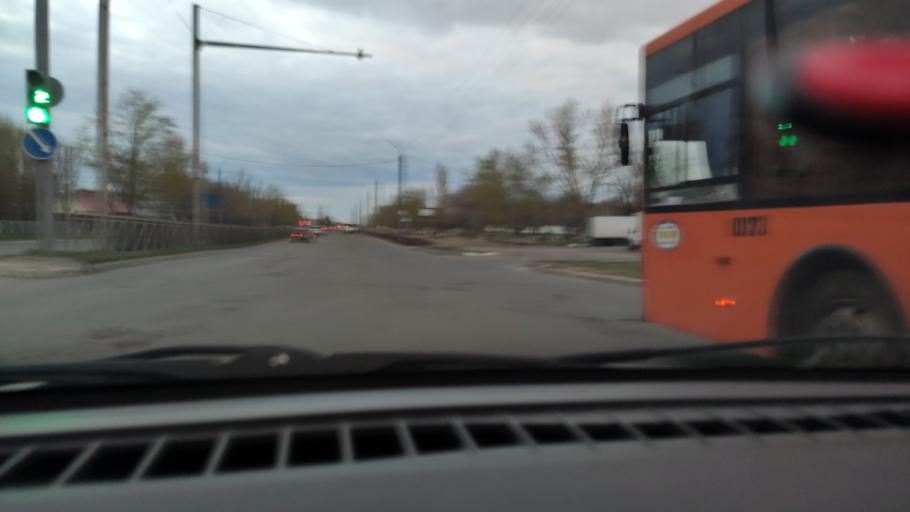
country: RU
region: Orenburg
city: Orenburg
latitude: 51.8187
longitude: 55.1076
